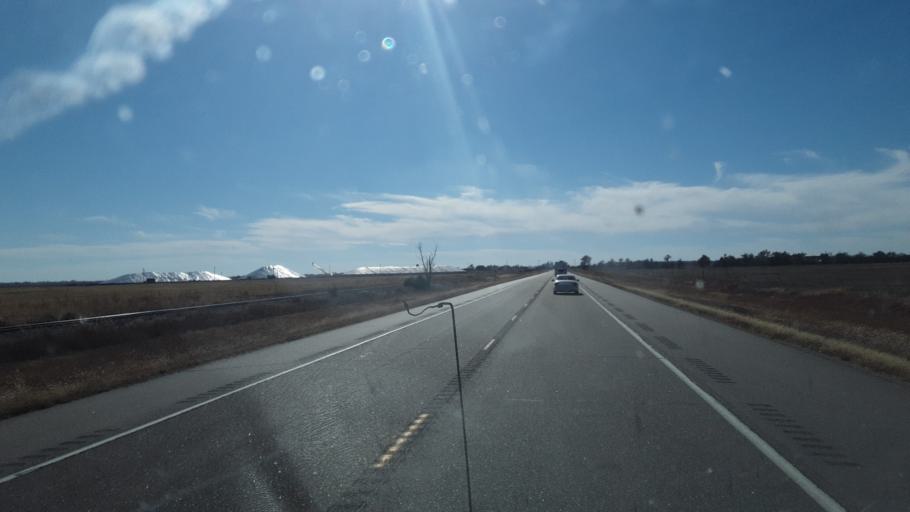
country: US
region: Kansas
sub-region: Pawnee County
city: Larned
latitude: 38.2082
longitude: -99.0600
